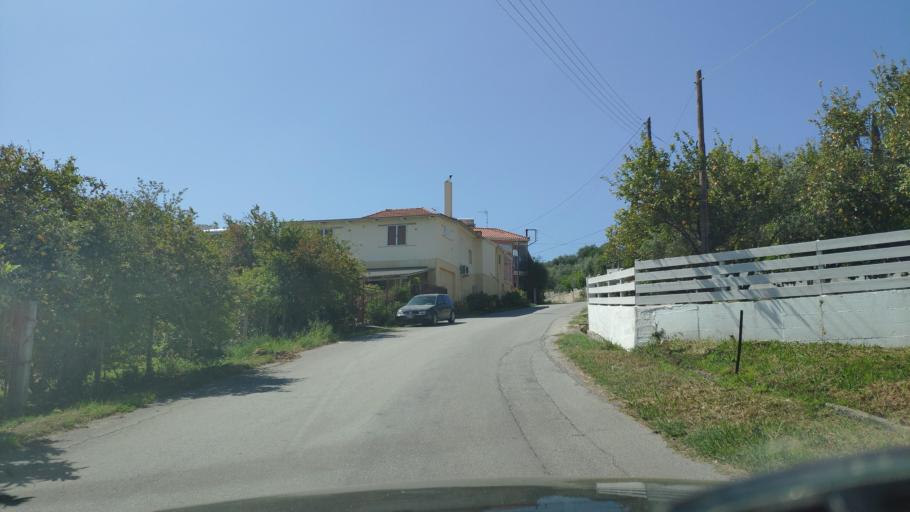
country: GR
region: West Greece
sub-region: Nomos Achaias
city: Aiyira
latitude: 38.1409
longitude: 22.3495
